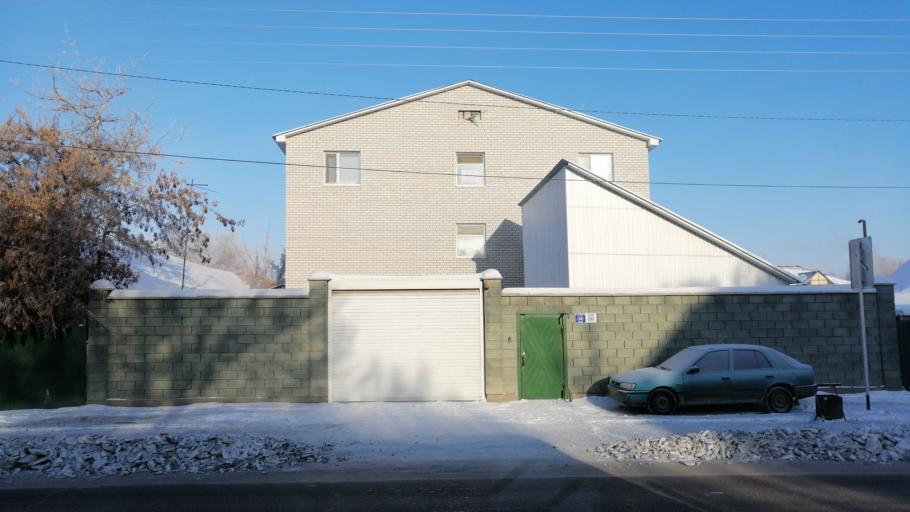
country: KZ
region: Aqtoebe
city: Aqtobe
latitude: 50.2990
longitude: 57.1461
